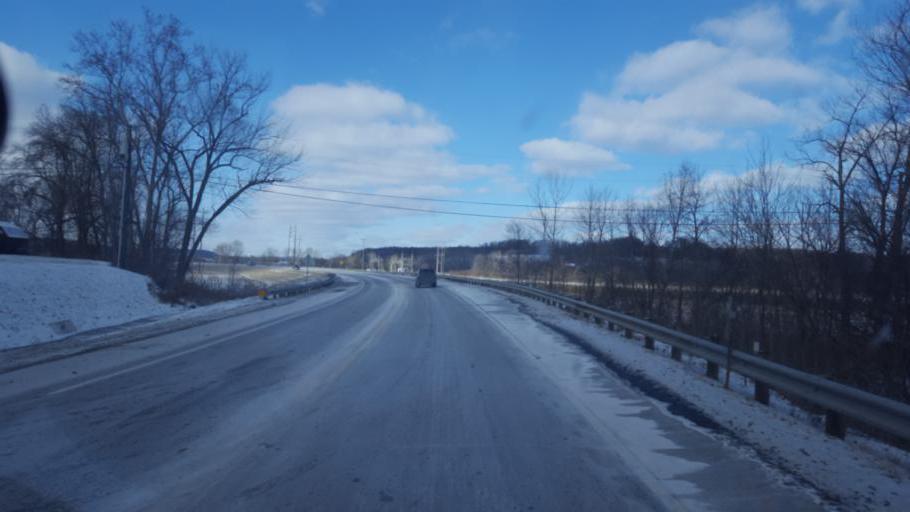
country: US
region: Ohio
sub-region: Coshocton County
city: Coshocton
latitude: 40.3009
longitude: -81.8954
